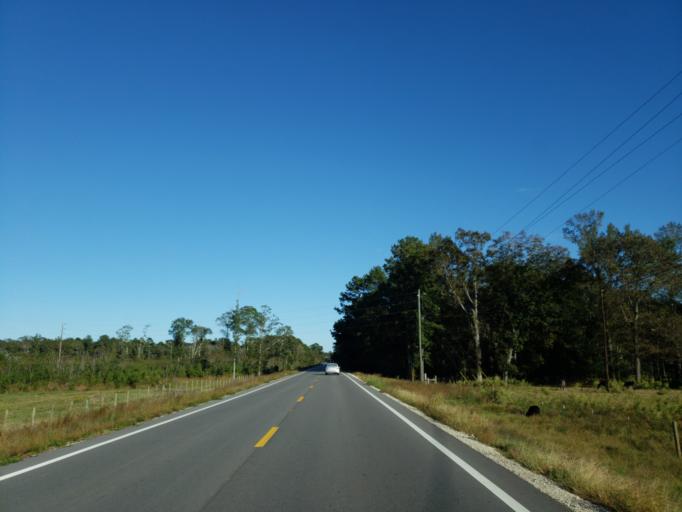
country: US
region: Mississippi
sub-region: Perry County
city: Richton
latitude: 31.3587
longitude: -89.0328
